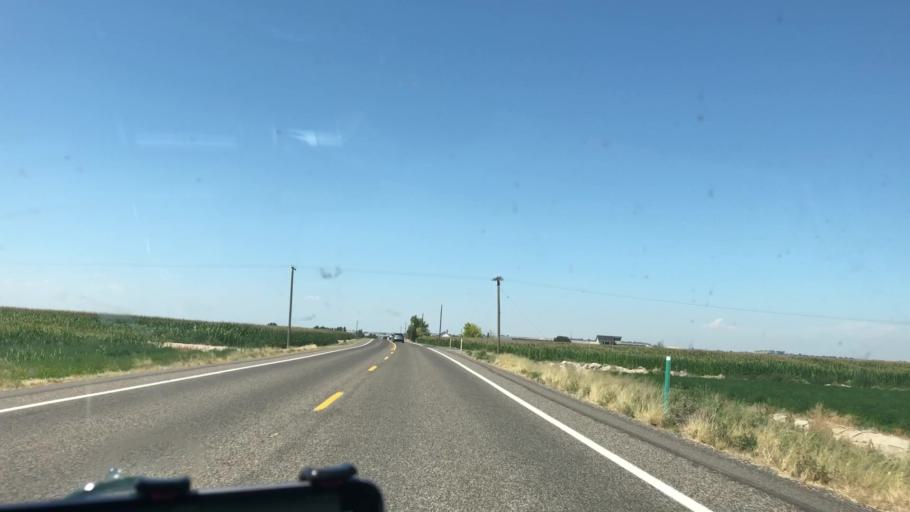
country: US
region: Idaho
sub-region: Owyhee County
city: Marsing
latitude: 43.5371
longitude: -116.8513
